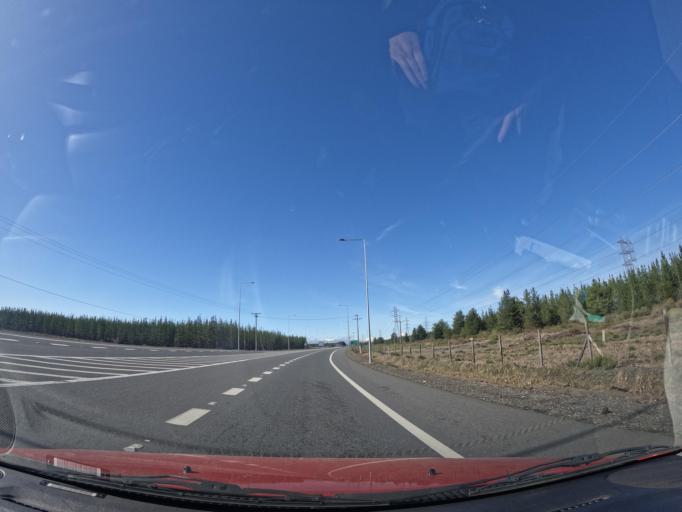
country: CL
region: Biobio
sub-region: Provincia de Biobio
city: Cabrero
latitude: -37.1378
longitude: -72.1762
